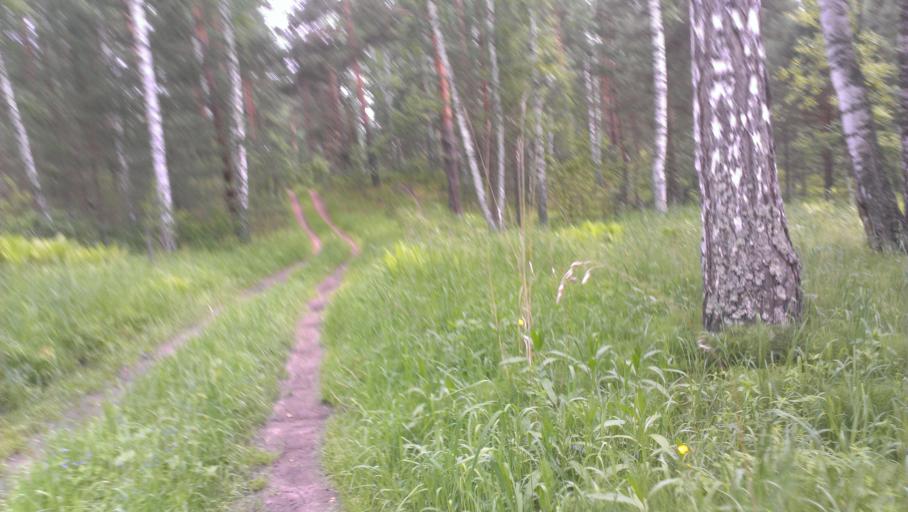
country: RU
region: Altai Krai
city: Sannikovo
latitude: 53.3481
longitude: 84.0393
